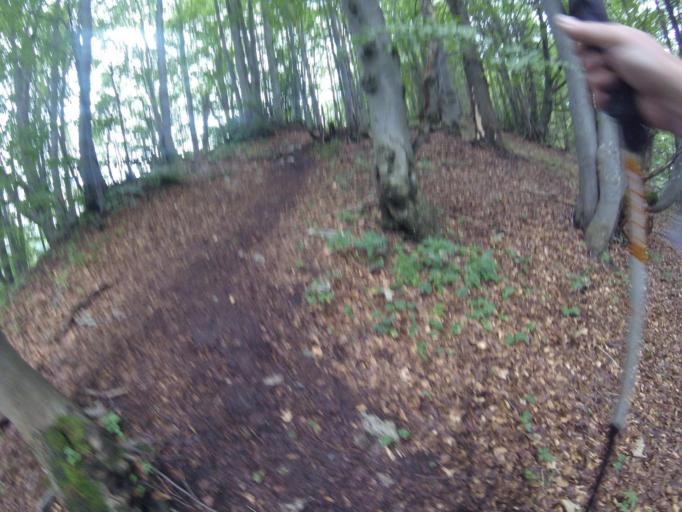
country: SK
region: Zilinsky
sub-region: Okres Zilina
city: Terchova
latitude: 49.2361
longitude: 19.0165
